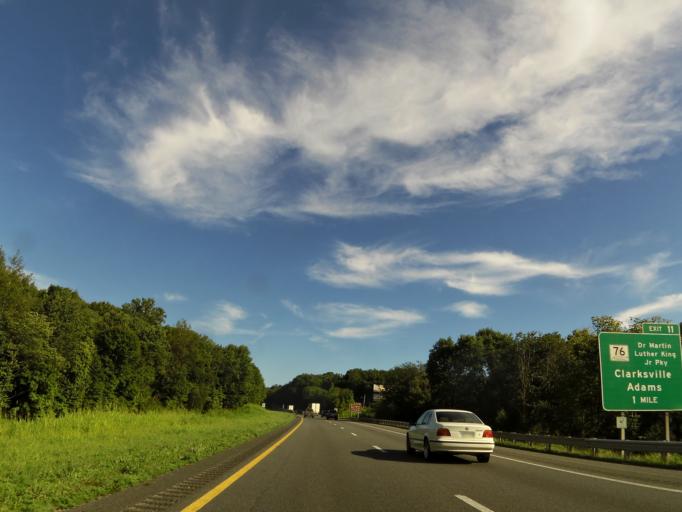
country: US
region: Tennessee
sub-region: Montgomery County
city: Clarksville
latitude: 36.5393
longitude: -87.2389
